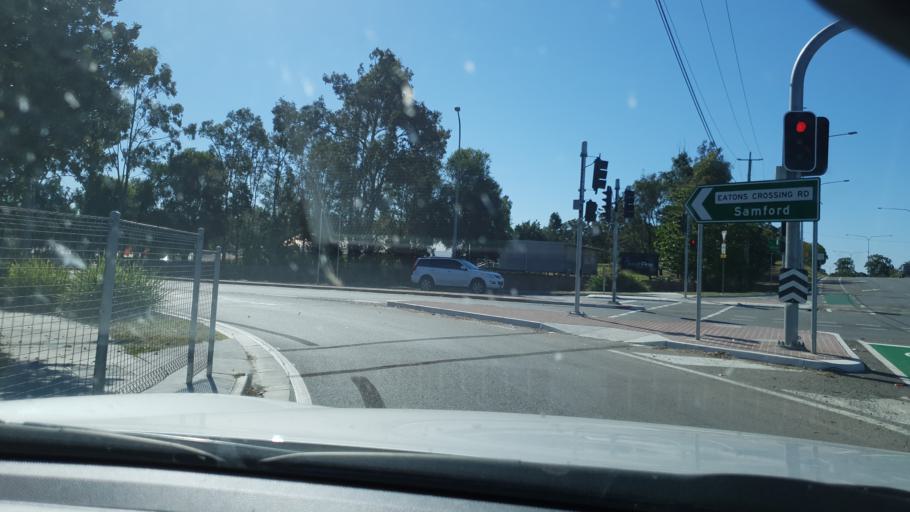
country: AU
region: Queensland
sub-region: Brisbane
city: Bridegman Downs
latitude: -27.3357
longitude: 152.9600
